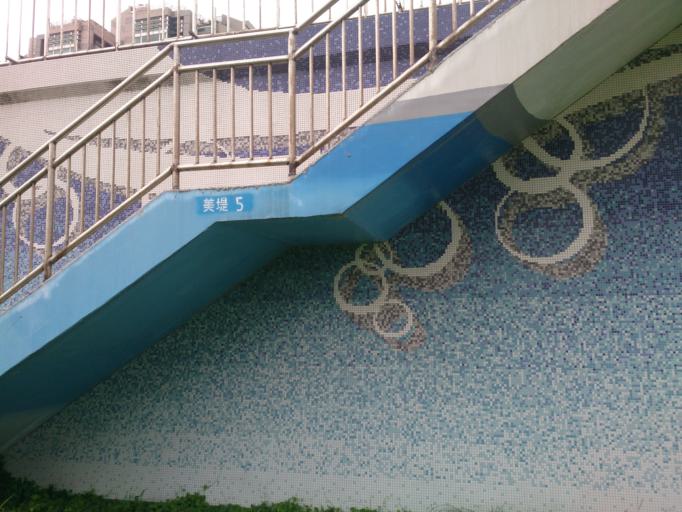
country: TW
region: Taipei
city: Taipei
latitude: 25.0764
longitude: 121.5662
